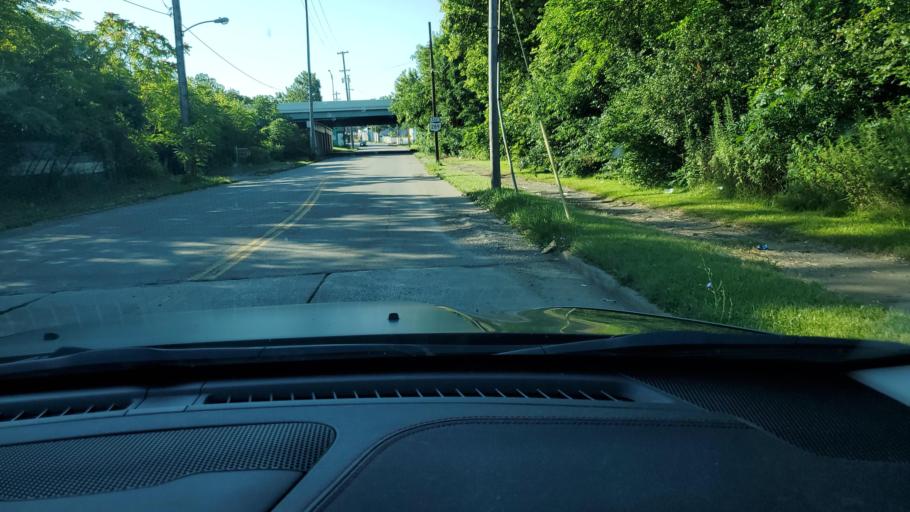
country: US
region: Ohio
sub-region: Mahoning County
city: Youngstown
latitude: 41.0957
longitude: -80.6382
